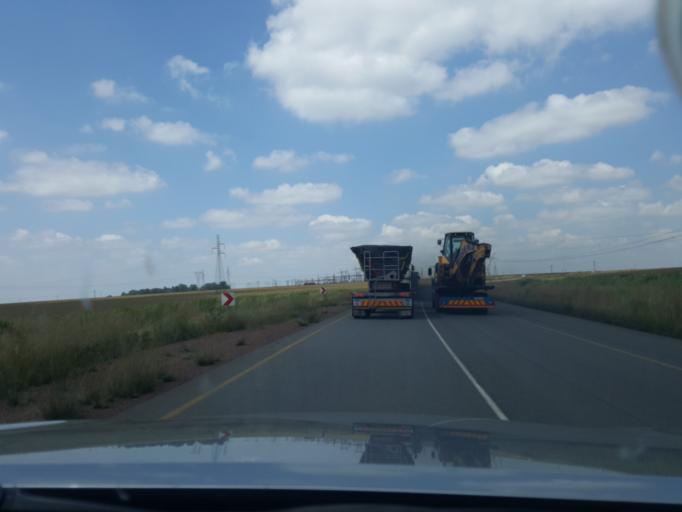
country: ZA
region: Mpumalanga
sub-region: Nkangala District Municipality
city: Witbank
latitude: -26.0140
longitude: 29.4136
